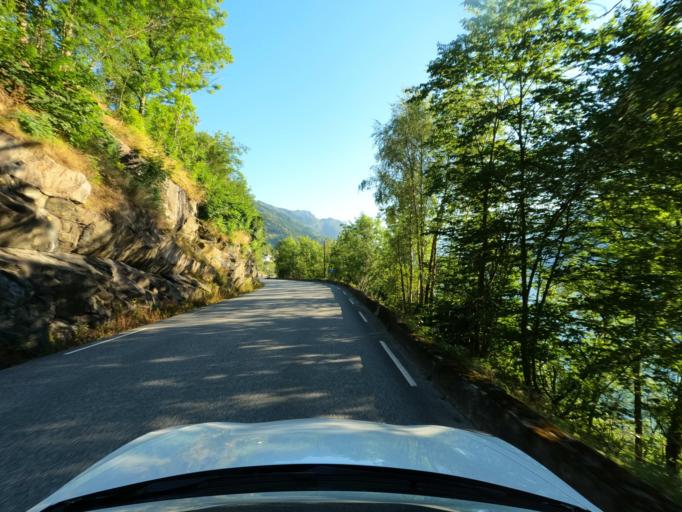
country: NO
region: Hordaland
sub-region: Odda
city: Odda
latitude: 60.2162
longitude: 6.6026
